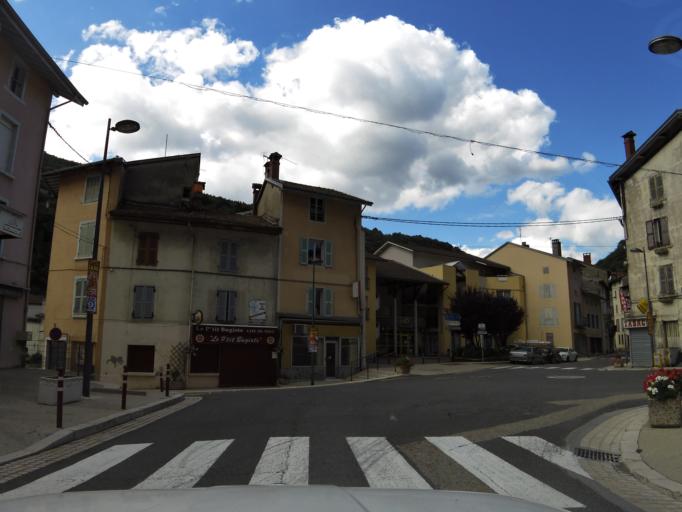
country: FR
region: Rhone-Alpes
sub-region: Departement de l'Ain
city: Tenay
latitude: 45.9189
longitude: 5.5097
